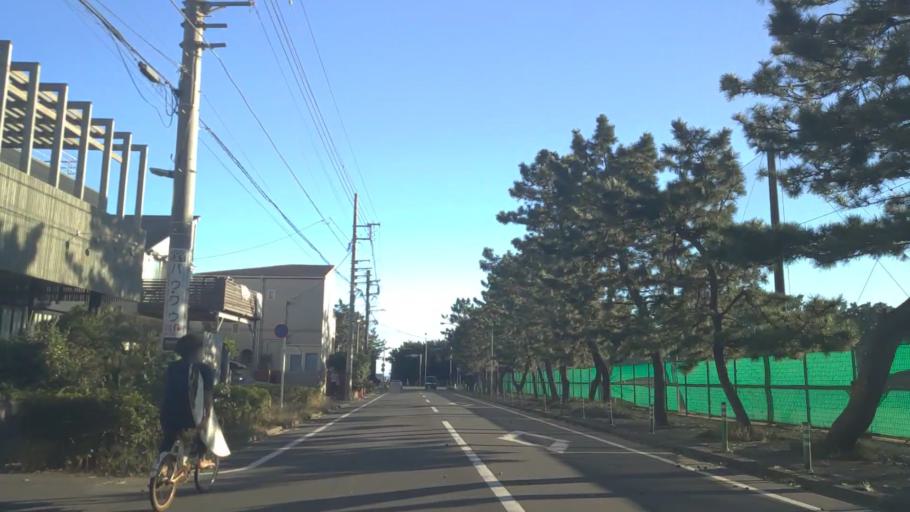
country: JP
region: Kanagawa
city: Chigasaki
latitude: 35.3193
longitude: 139.4152
